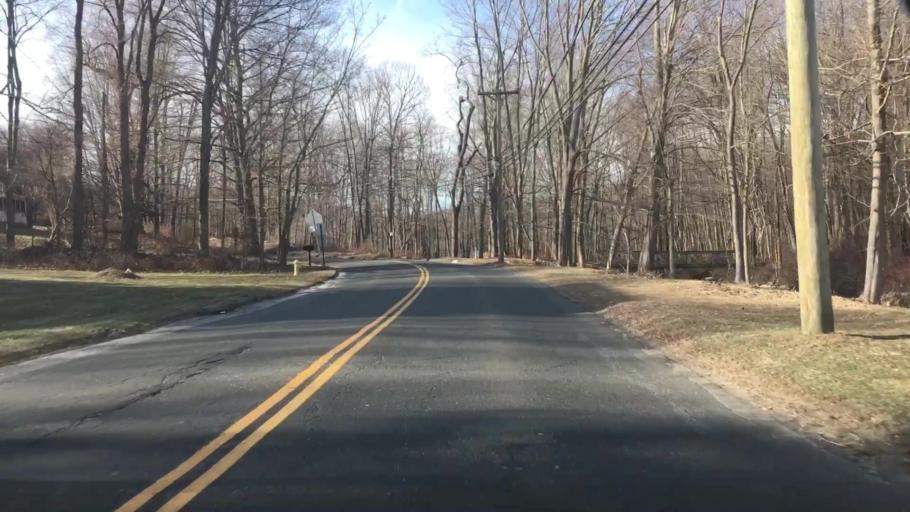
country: US
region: Connecticut
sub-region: Fairfield County
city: Danbury
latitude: 41.3675
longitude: -73.4957
